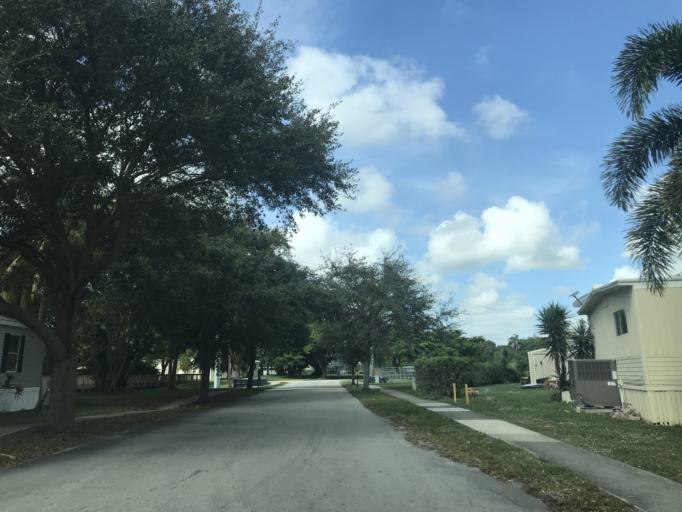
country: US
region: Florida
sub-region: Palm Beach County
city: Boca Pointe
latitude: 26.3119
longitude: -80.1764
